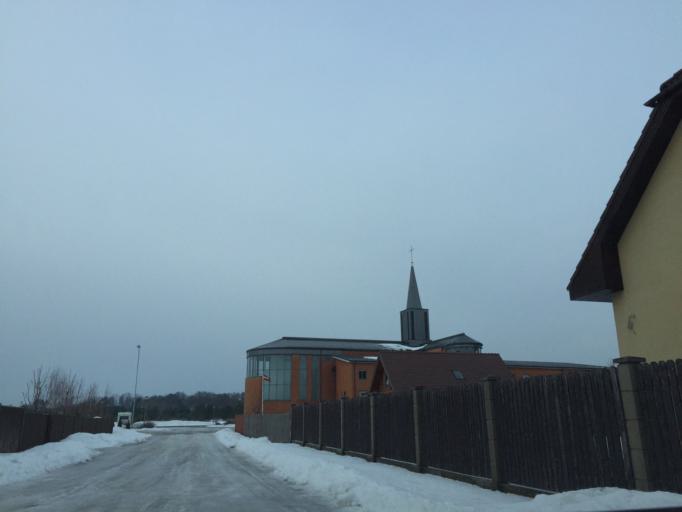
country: LV
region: Ikskile
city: Ikskile
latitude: 56.8406
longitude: 24.4783
